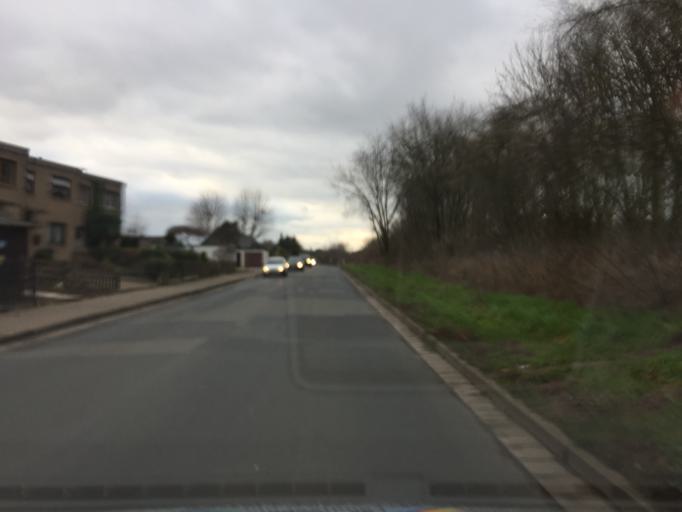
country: DE
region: Lower Saxony
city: Stolzenau
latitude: 52.5230
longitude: 9.0683
